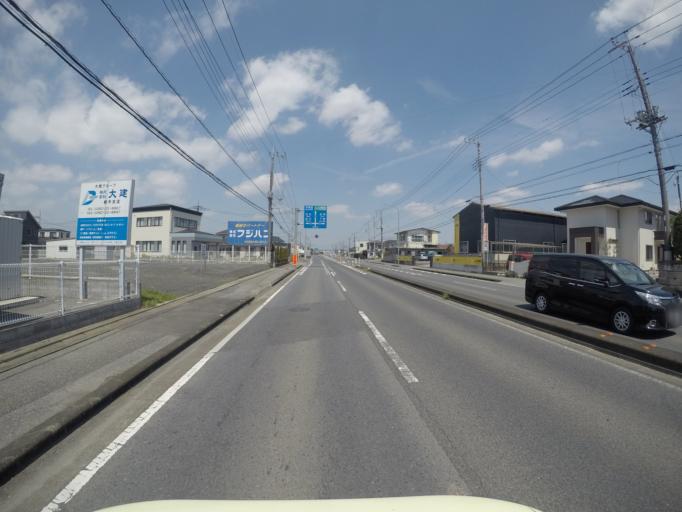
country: JP
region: Tochigi
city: Mibu
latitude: 36.4284
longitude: 139.7951
